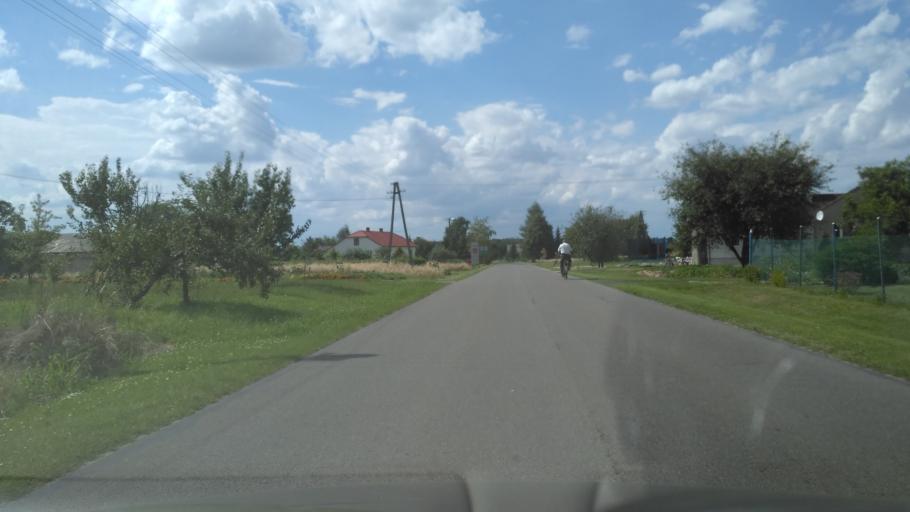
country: PL
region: Lublin Voivodeship
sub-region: Powiat leczynski
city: Milejow
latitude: 51.1858
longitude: 22.9487
